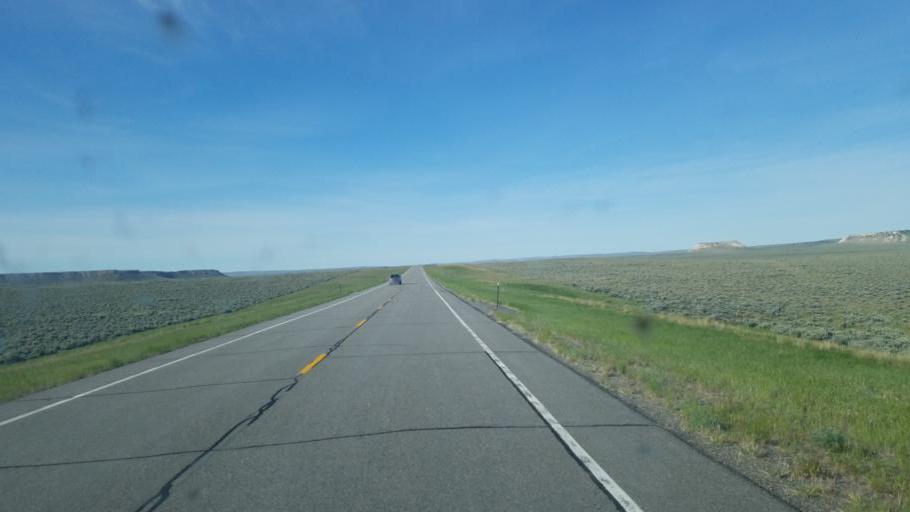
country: US
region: Wyoming
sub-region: Fremont County
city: Riverton
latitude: 42.6692
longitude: -108.1818
